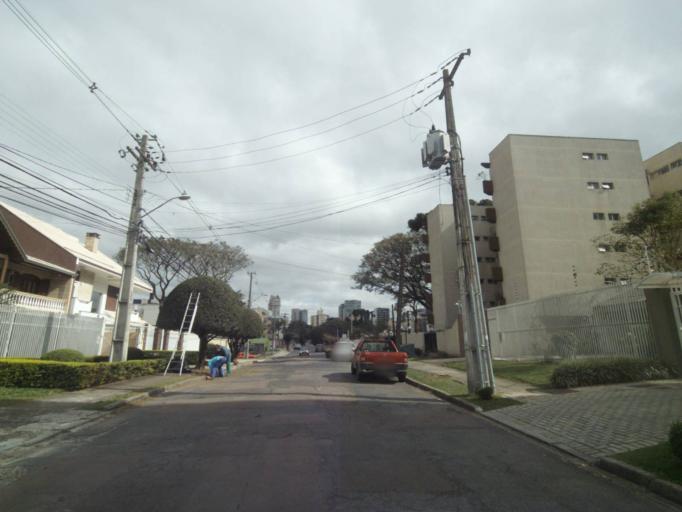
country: BR
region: Parana
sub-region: Curitiba
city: Curitiba
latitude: -25.4609
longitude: -49.2820
